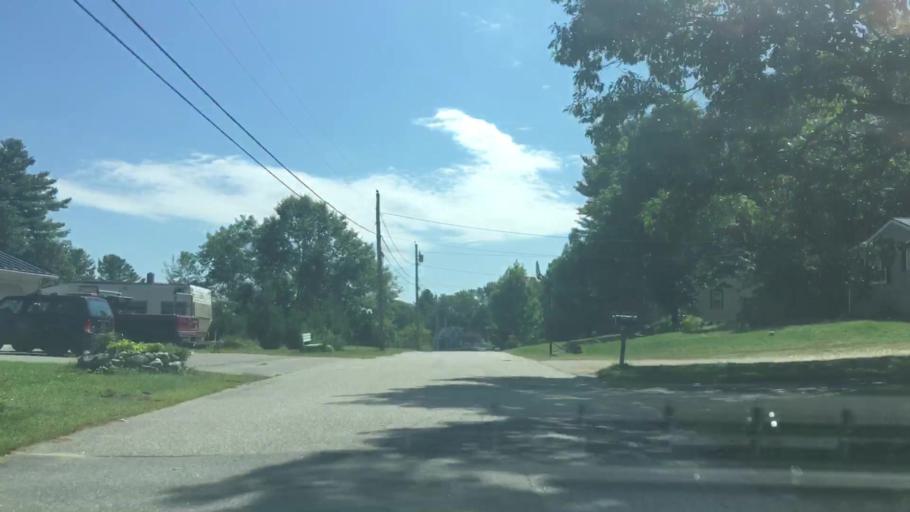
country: US
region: Maine
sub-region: Androscoggin County
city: Sabattus
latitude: 44.1037
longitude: -70.1310
